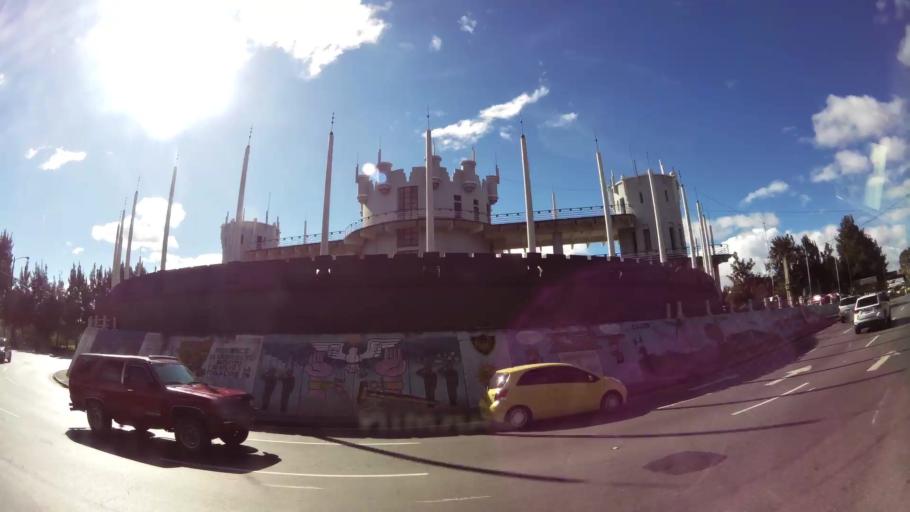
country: GT
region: Guatemala
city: Guatemala City
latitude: 14.6136
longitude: -90.5041
